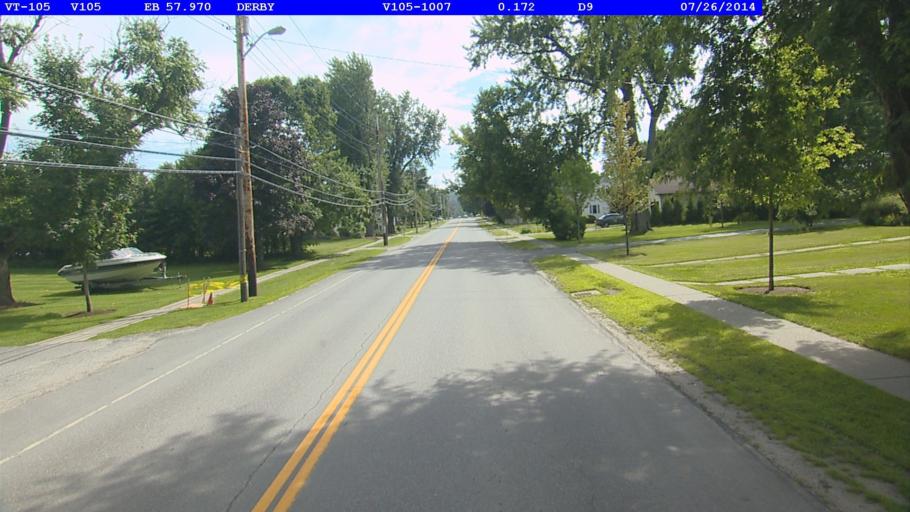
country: US
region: Vermont
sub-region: Orleans County
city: Newport
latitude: 44.9521
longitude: -72.1315
